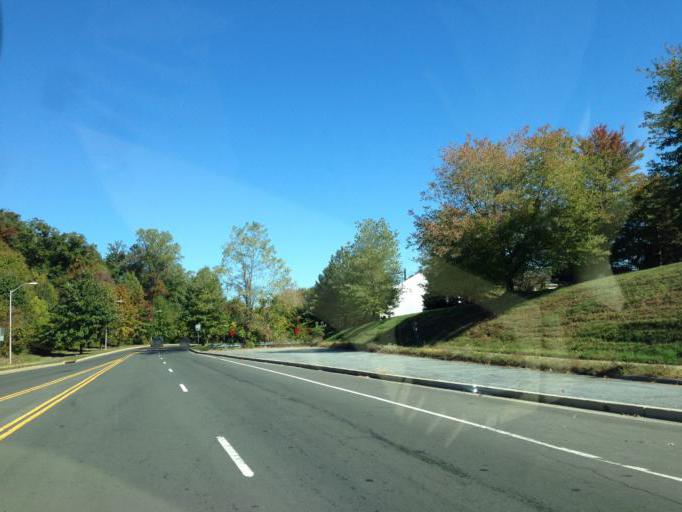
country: US
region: Maryland
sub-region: Montgomery County
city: Germantown
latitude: 39.1922
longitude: -77.2422
